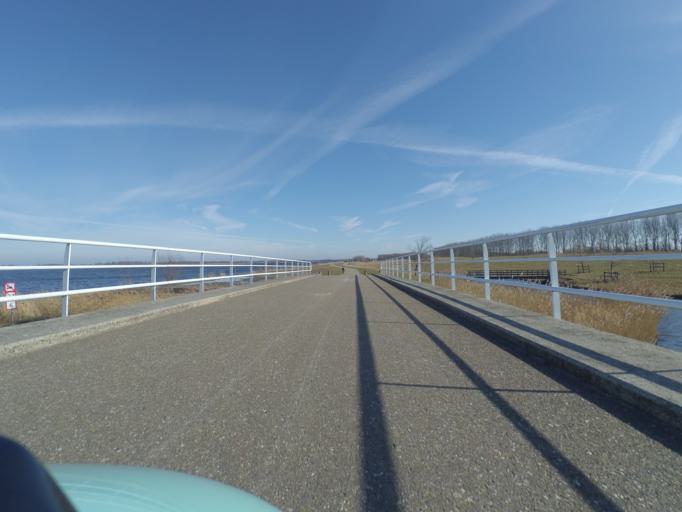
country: NL
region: Flevoland
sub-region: Gemeente Almere
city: Almere Stad
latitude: 52.3858
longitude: 5.1873
